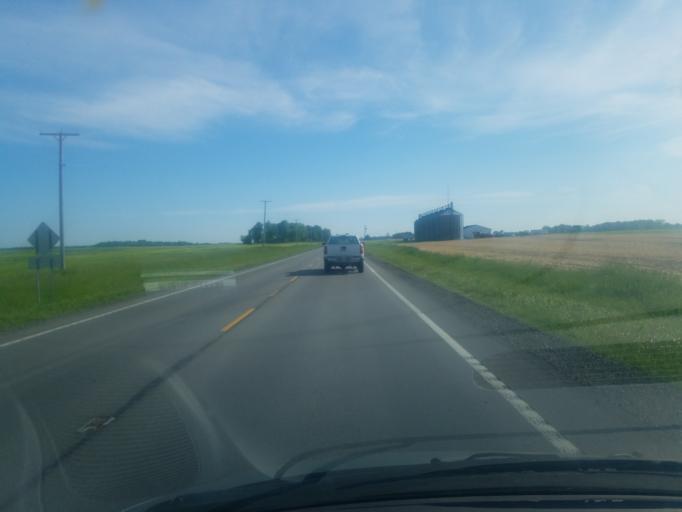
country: US
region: Ohio
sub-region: Crawford County
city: Bucyrus
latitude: 40.7359
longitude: -83.0419
